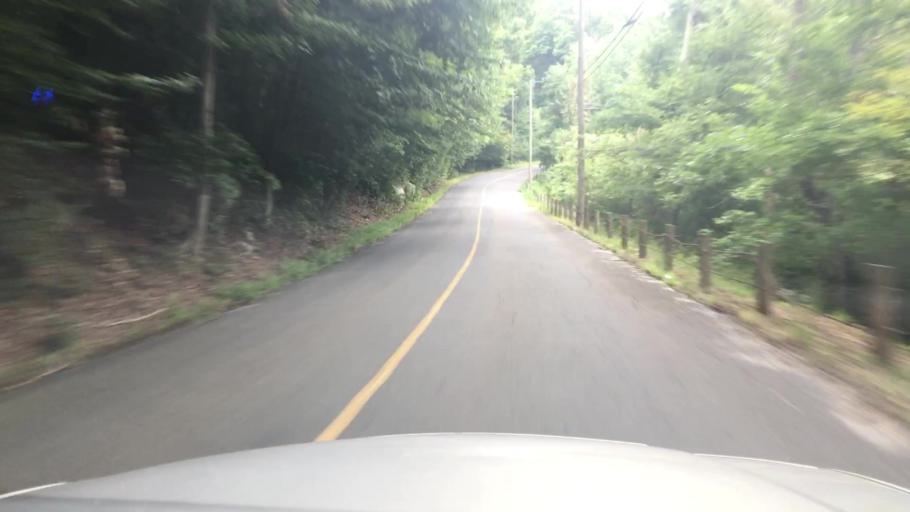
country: US
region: Connecticut
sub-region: Middlesex County
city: Deep River Center
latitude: 41.3854
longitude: -72.4160
